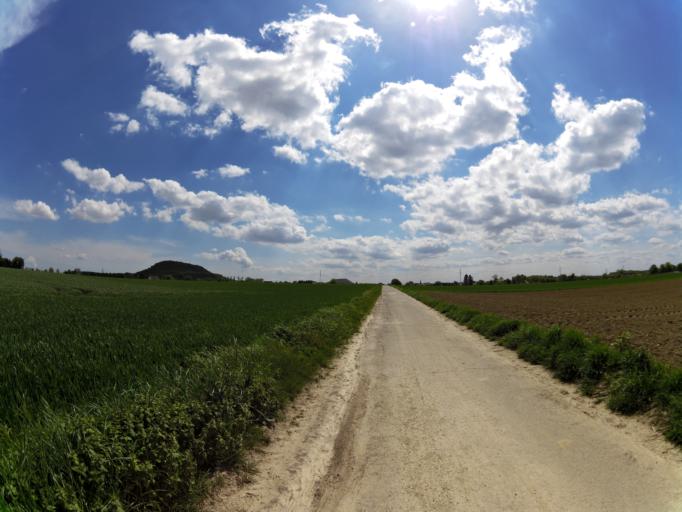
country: DE
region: North Rhine-Westphalia
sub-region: Regierungsbezirk Koln
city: Herzogenrath
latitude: 50.8950
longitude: 6.0877
